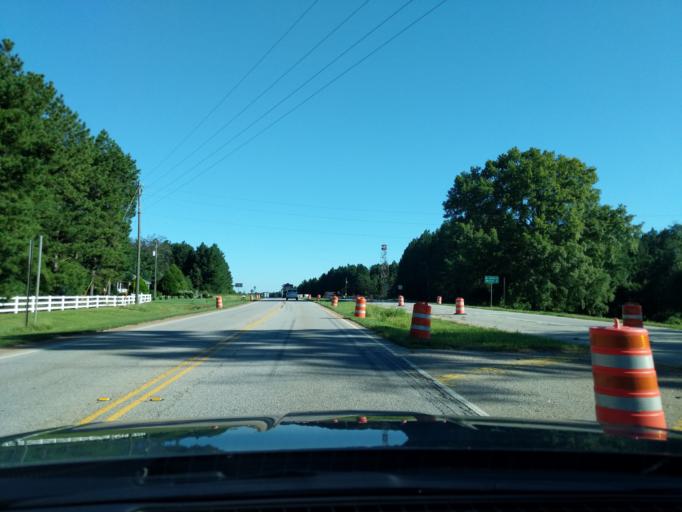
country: US
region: Georgia
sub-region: McDuffie County
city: Thomson
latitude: 33.5470
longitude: -82.5095
